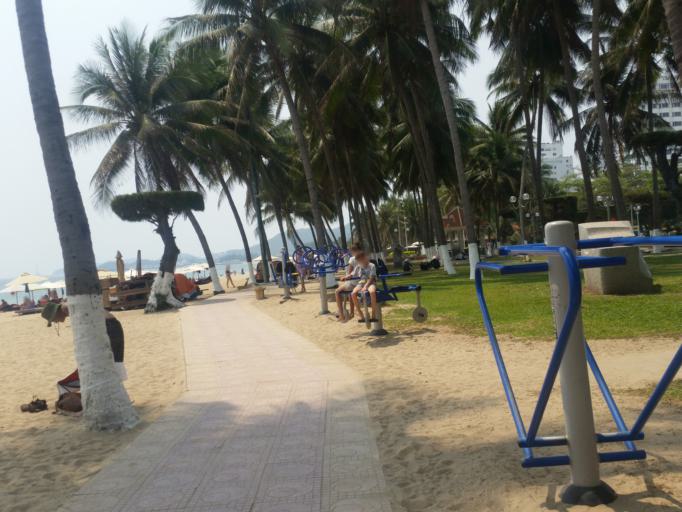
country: VN
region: Khanh Hoa
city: Nha Trang
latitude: 12.2331
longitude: 109.1984
